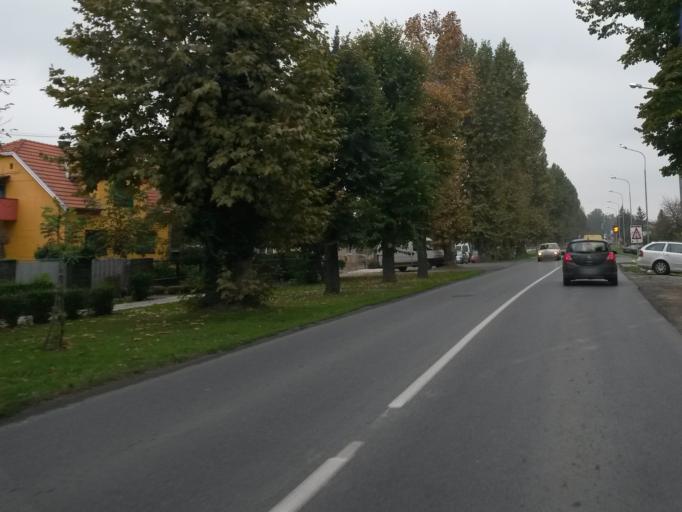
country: HR
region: Osjecko-Baranjska
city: Visnjevac
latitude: 45.5329
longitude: 18.6283
